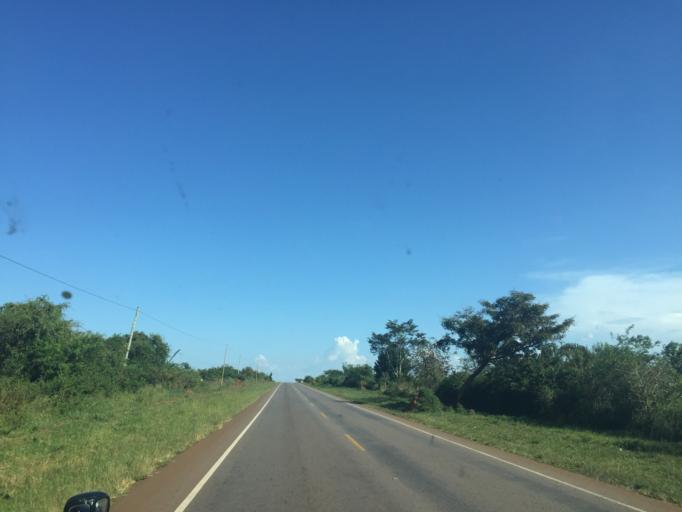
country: UG
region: Central Region
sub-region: Nakasongola District
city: Nakasongola
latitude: 1.3710
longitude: 32.3528
